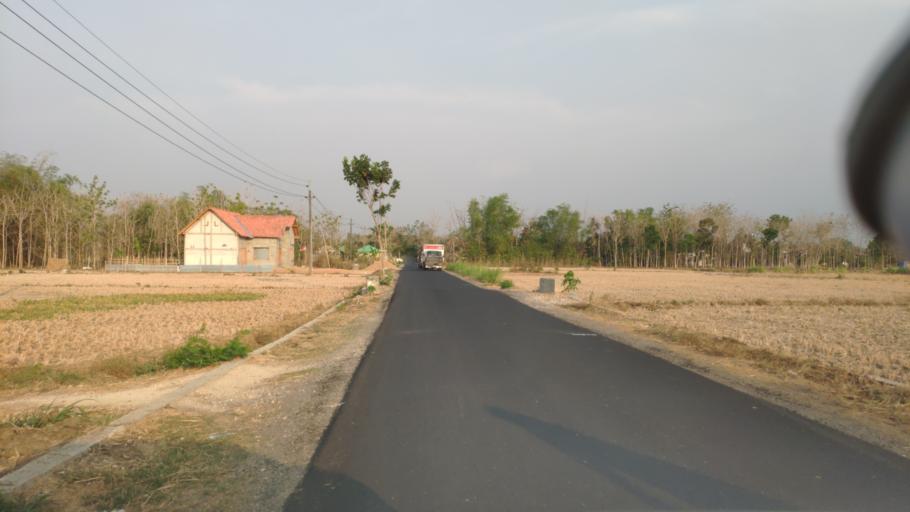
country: ID
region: Central Java
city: Kunden
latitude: -6.9543
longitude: 111.4066
